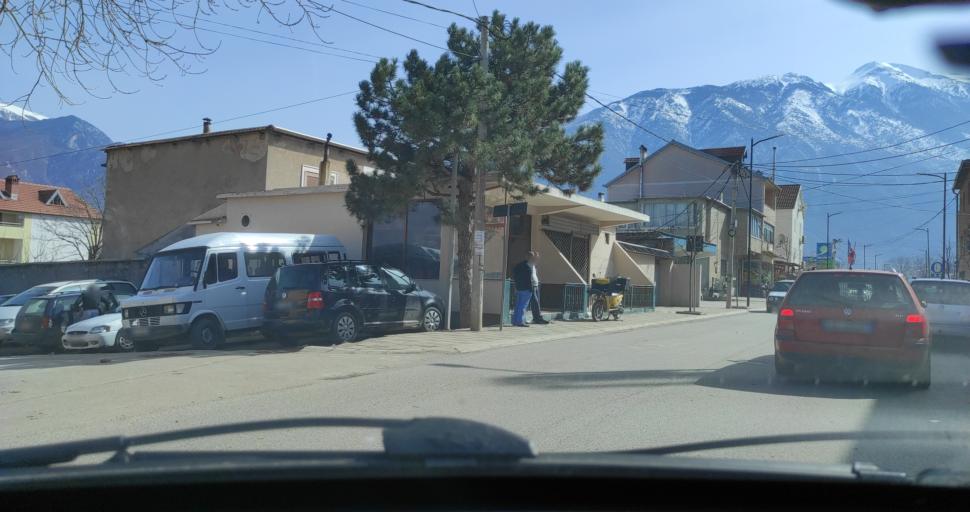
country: AL
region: Kukes
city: Kukes
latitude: 42.0755
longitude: 20.4266
